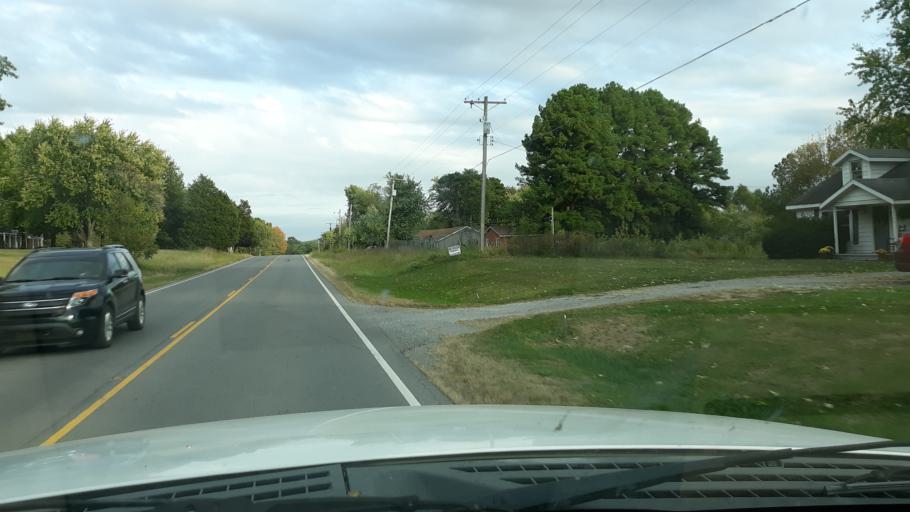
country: US
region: Illinois
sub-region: Saline County
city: Eldorado
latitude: 37.8233
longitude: -88.5008
